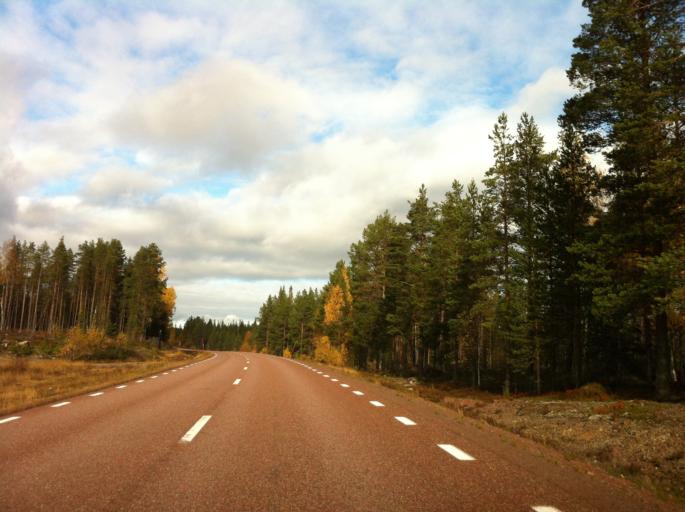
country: SE
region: Dalarna
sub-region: Alvdalens Kommun
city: AElvdalen
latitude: 61.5170
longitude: 13.3674
